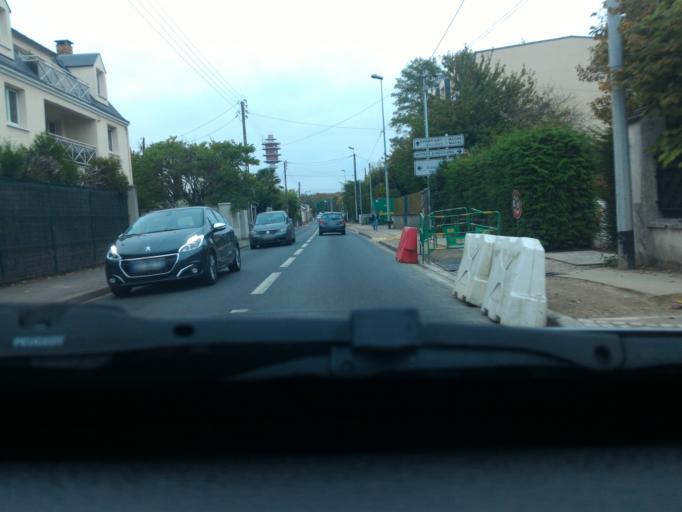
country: FR
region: Ile-de-France
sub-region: Departement du Val-de-Marne
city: Chennevieres-sur-Marne
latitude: 48.7970
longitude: 2.5337
